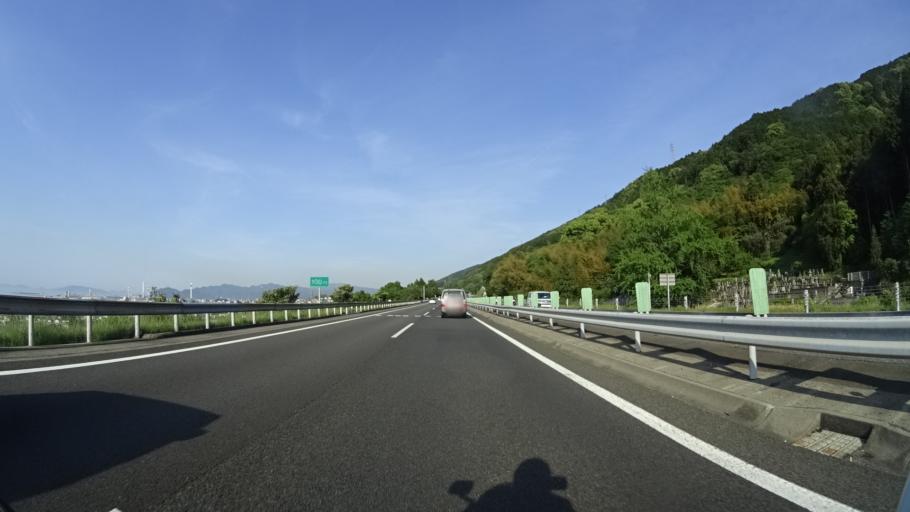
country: JP
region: Ehime
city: Kawanoecho
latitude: 33.9616
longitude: 133.5140
